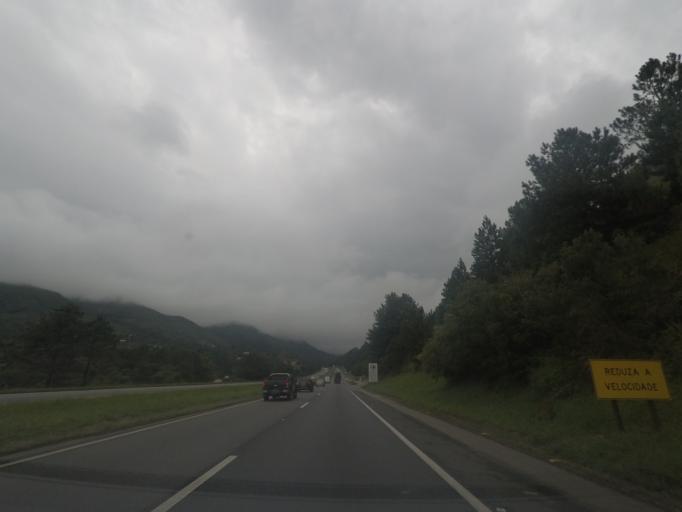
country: BR
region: Parana
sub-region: Campina Grande Do Sul
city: Campina Grande do Sul
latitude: -25.1296
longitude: -48.8575
